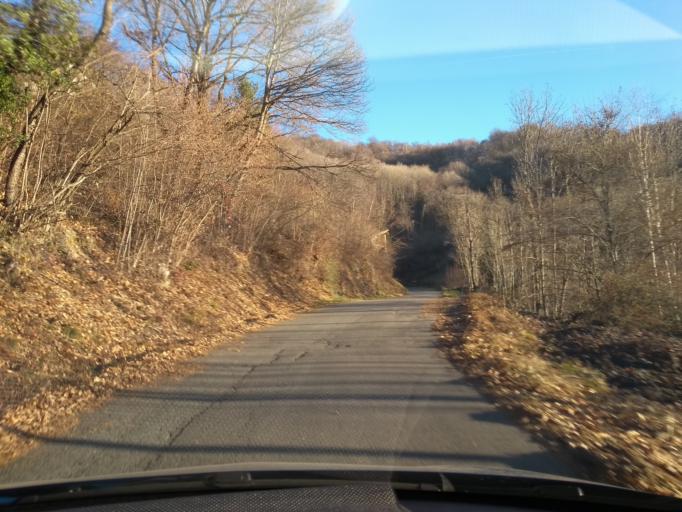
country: IT
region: Piedmont
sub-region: Provincia di Torino
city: Corio
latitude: 45.3229
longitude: 7.5422
